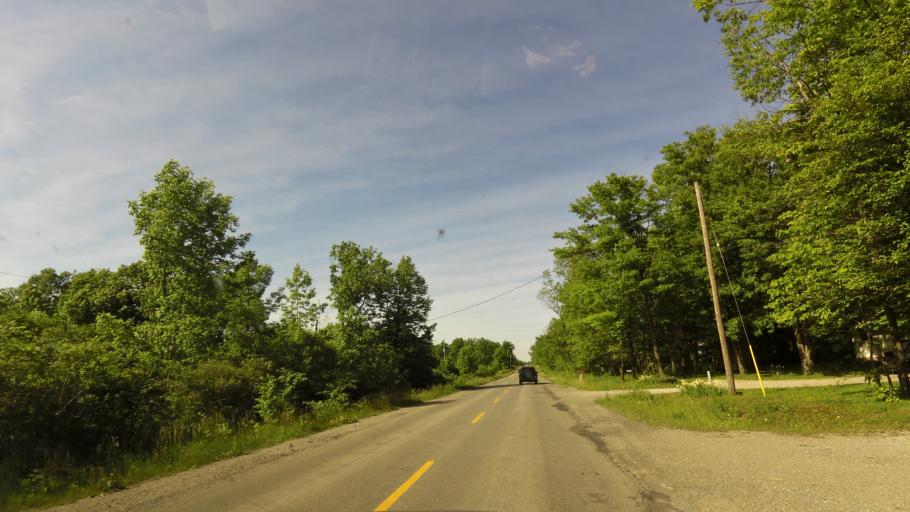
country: CA
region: Ontario
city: Ancaster
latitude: 43.0450
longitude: -80.0326
